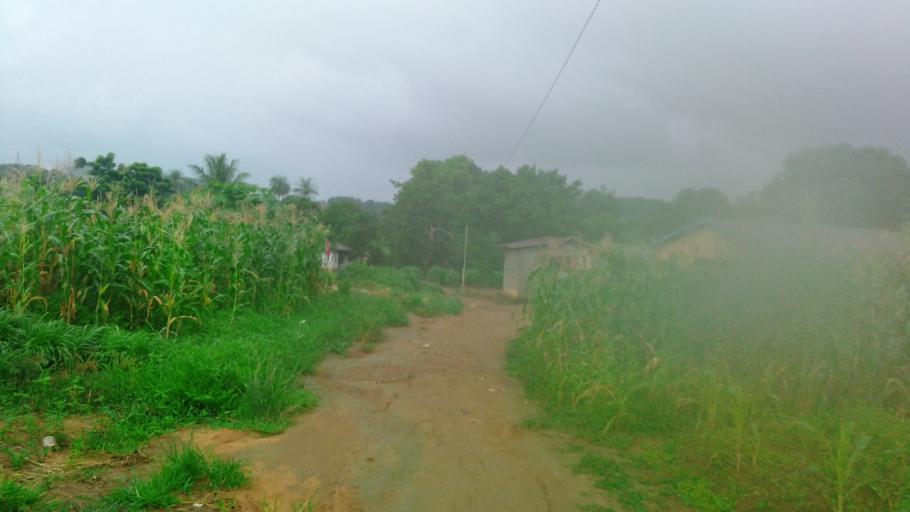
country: SL
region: Northern Province
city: Lunsar
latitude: 8.6849
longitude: -12.5271
